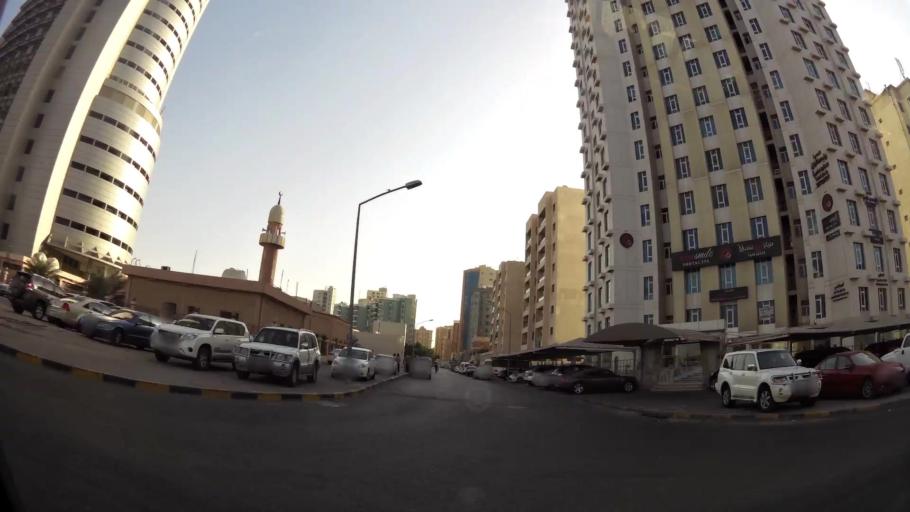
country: KW
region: Muhafazat Hawalli
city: As Salimiyah
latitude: 29.3338
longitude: 48.0918
